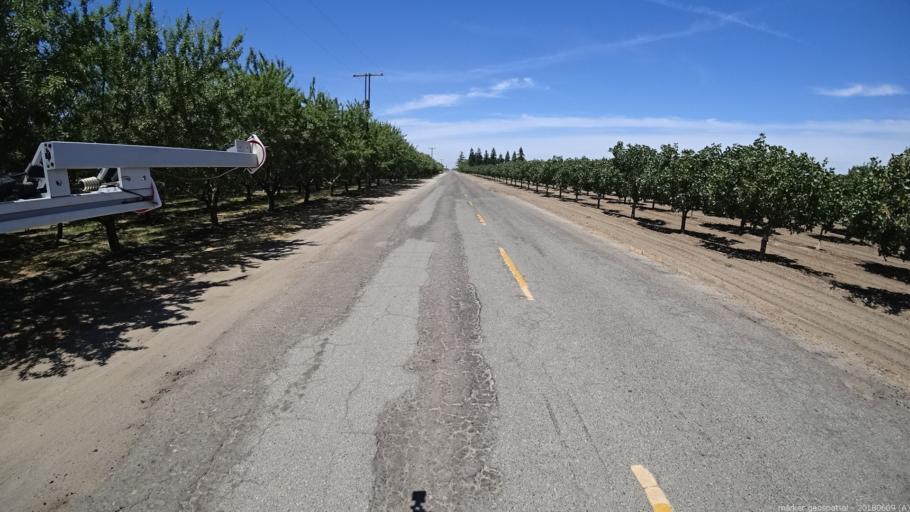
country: US
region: California
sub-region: Madera County
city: Madera
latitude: 36.9383
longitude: -120.1390
